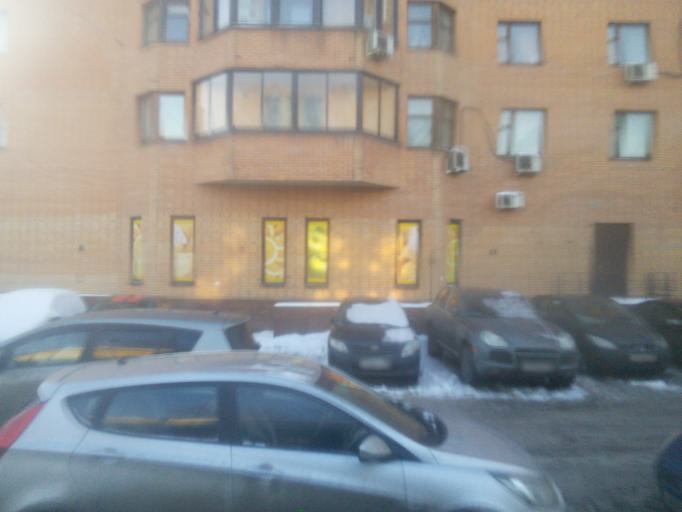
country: RU
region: Moscow
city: Lefortovo
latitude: 55.7651
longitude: 37.6704
